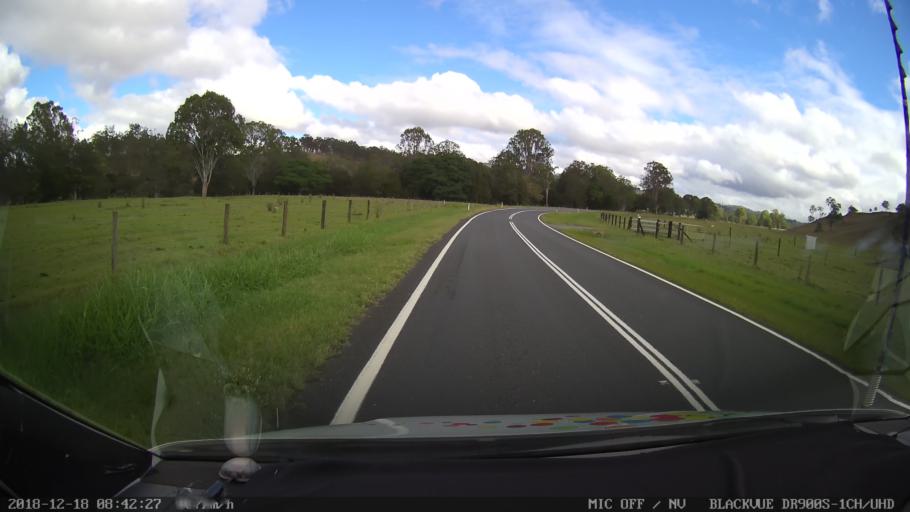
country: AU
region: Queensland
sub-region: Logan
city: Cedar Vale
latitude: -28.2269
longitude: 152.8594
